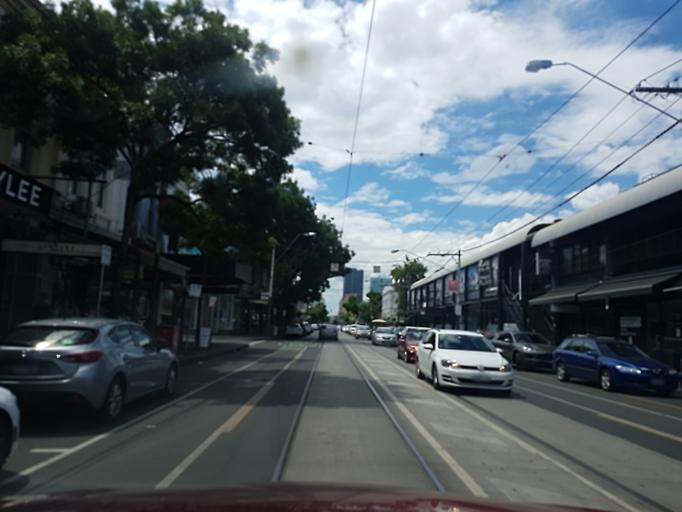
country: AU
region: Victoria
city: Windsor
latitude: -37.8456
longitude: 144.9945
